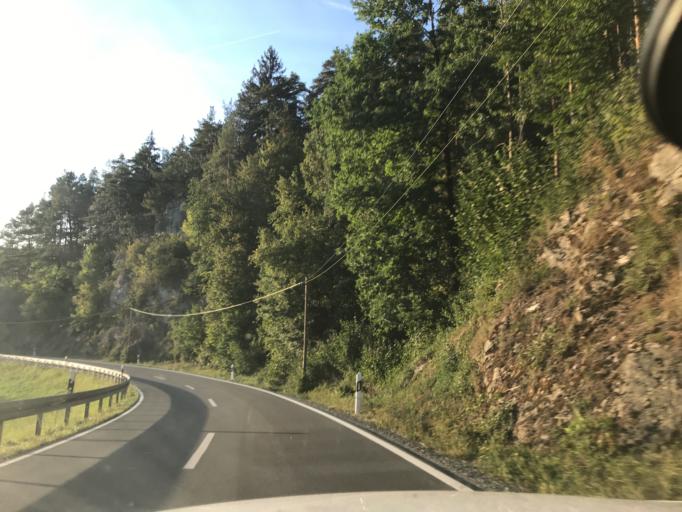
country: DE
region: Bavaria
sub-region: Upper Franconia
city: Pegnitz
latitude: 49.7310
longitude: 11.5576
